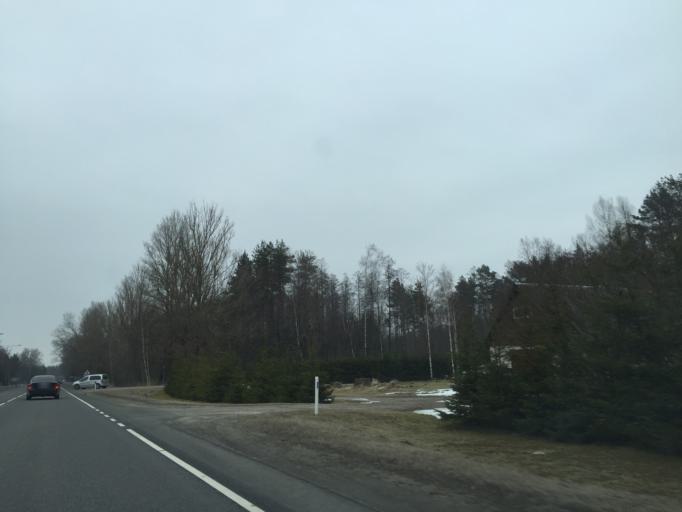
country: EE
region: Paernumaa
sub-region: Paernu linn
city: Parnu
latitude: 58.2424
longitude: 24.5132
